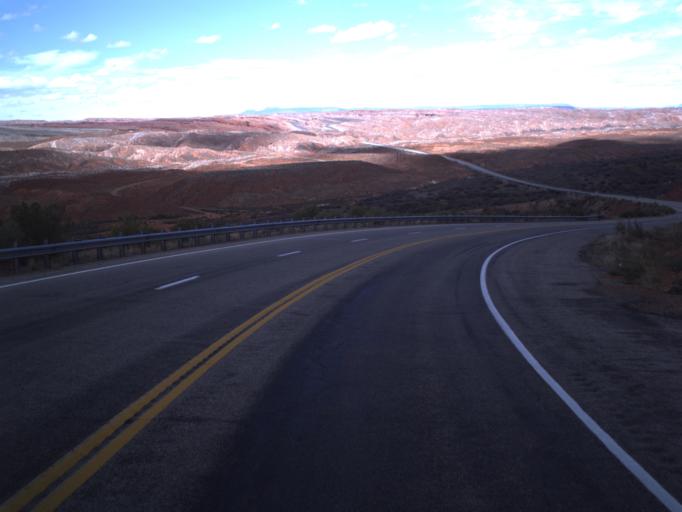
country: US
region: Utah
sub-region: San Juan County
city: Blanding
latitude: 37.2607
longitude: -109.6739
